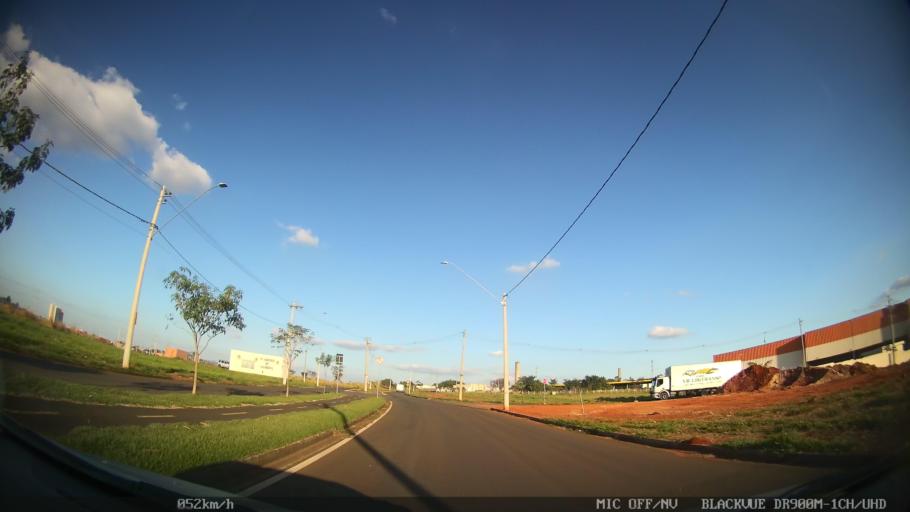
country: BR
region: Sao Paulo
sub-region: Santa Barbara D'Oeste
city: Santa Barbara d'Oeste
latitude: -22.7512
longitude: -47.3875
